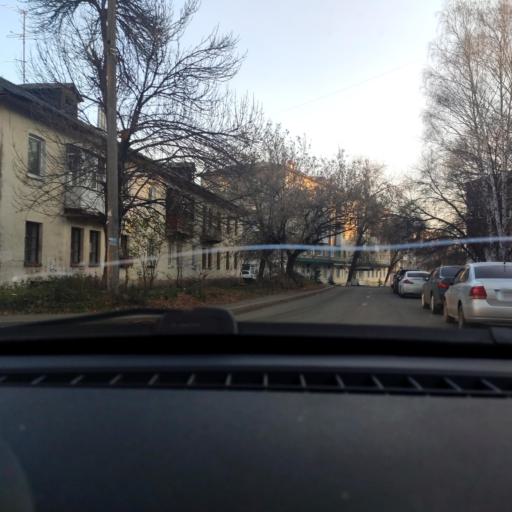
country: RU
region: Bashkortostan
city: Ufa
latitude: 54.8137
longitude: 56.1155
